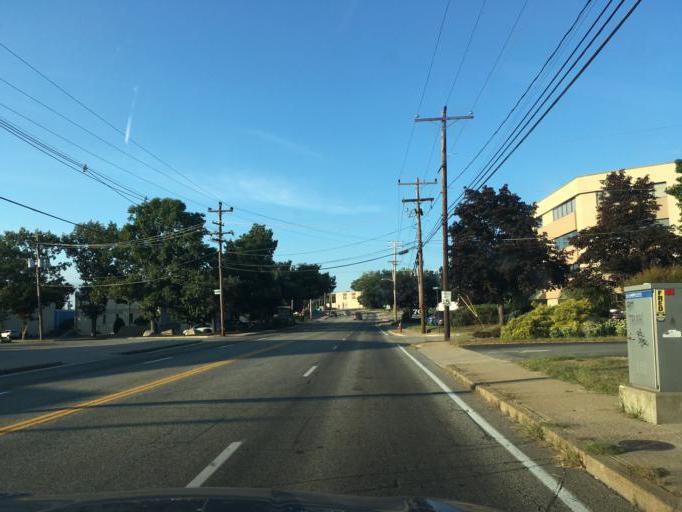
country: US
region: Rhode Island
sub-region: Providence County
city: Cranston
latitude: 41.7490
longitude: -71.4357
